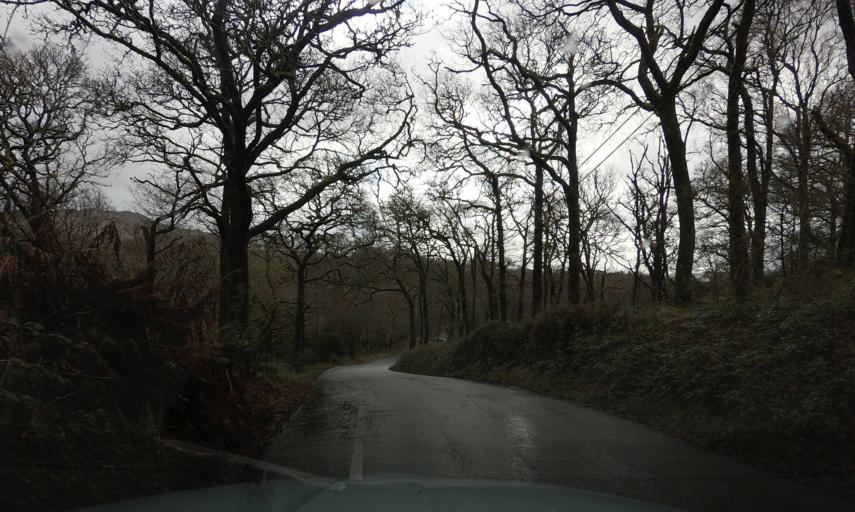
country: GB
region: Scotland
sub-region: West Dunbartonshire
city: Balloch
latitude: 56.1062
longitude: -4.5694
